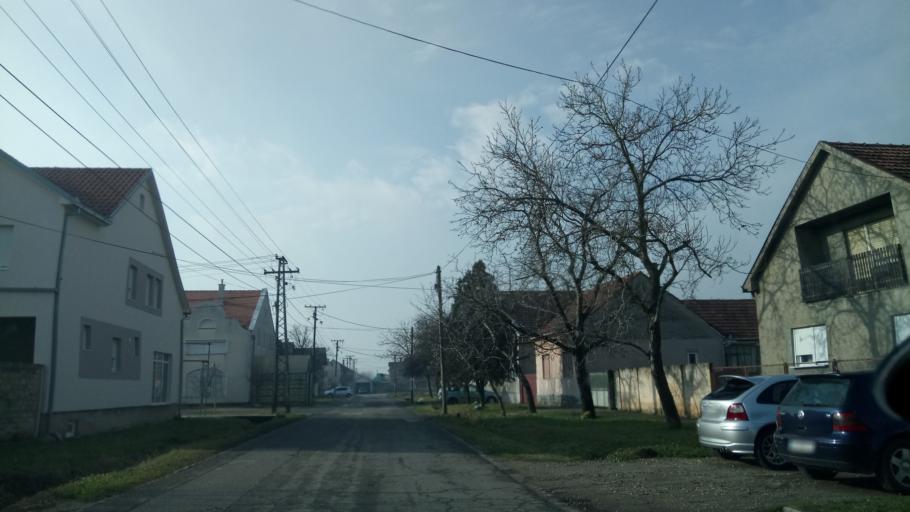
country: RS
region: Autonomna Pokrajina Vojvodina
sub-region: Sremski Okrug
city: Stara Pazova
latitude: 44.9827
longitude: 20.1728
